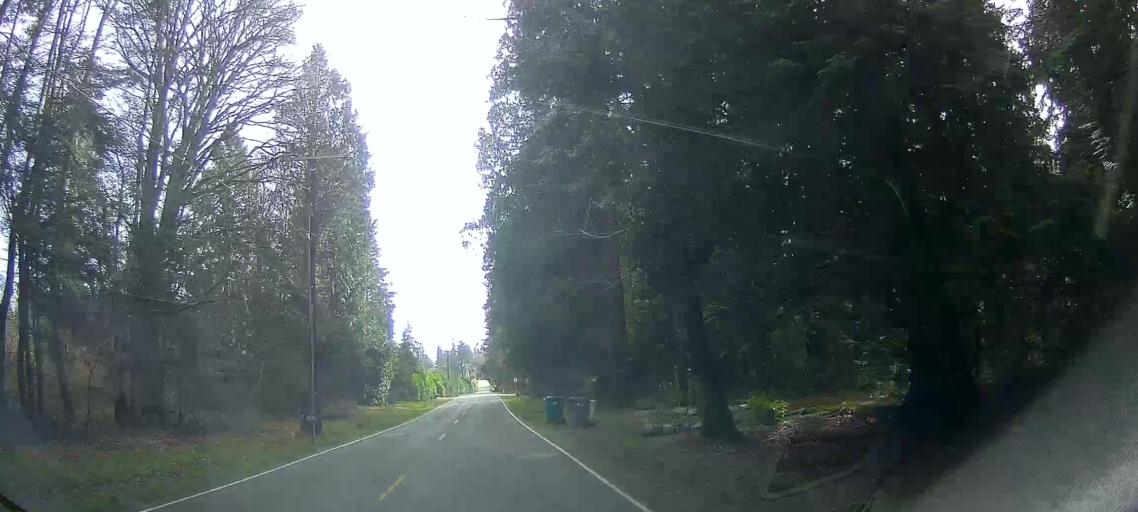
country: US
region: Washington
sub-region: Island County
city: Langley
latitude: 48.0989
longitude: -122.4151
